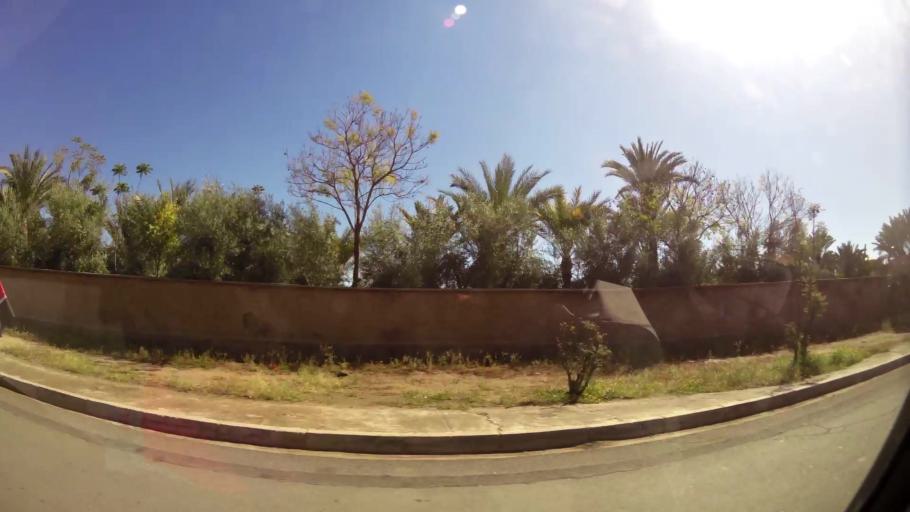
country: MA
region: Marrakech-Tensift-Al Haouz
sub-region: Marrakech
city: Marrakesh
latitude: 31.6483
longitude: -7.9776
